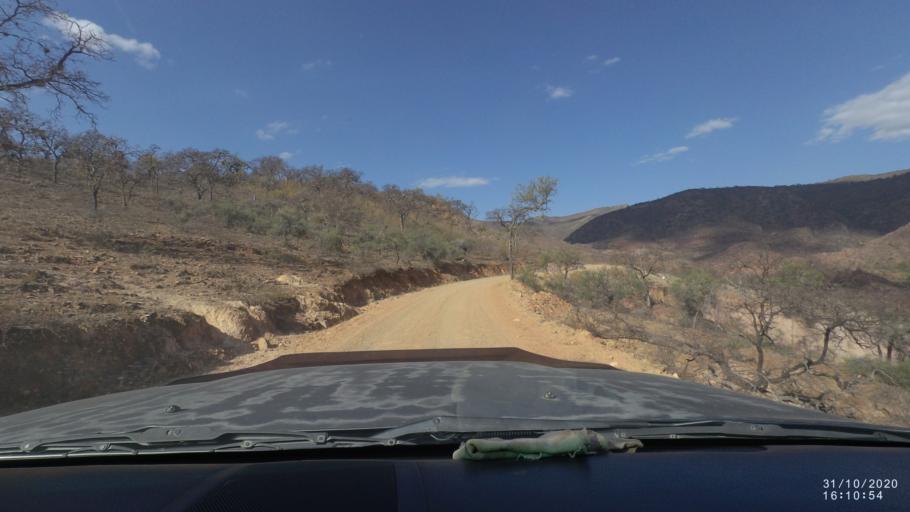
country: BO
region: Chuquisaca
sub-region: Provincia Zudanez
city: Mojocoya
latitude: -18.3815
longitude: -64.6267
